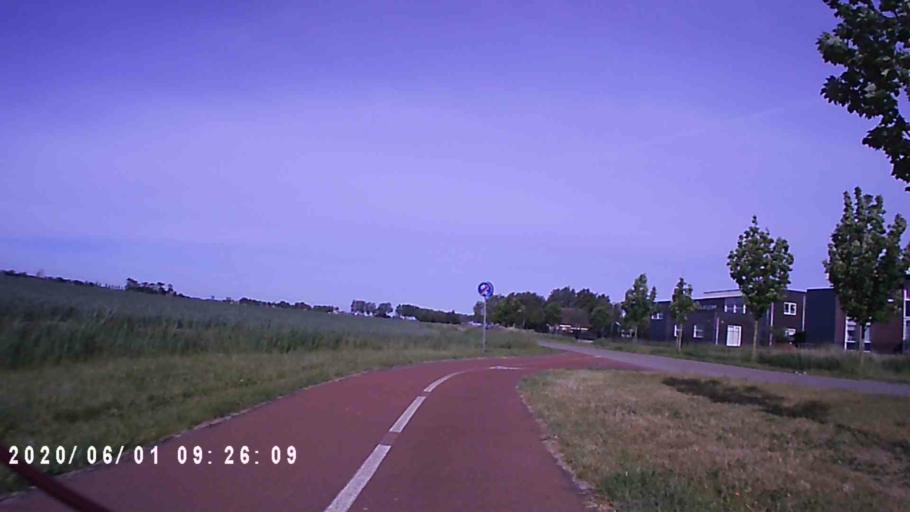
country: NL
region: Friesland
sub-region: Gemeente Leeuwarderadeel
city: Stiens
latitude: 53.2655
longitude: 5.7474
